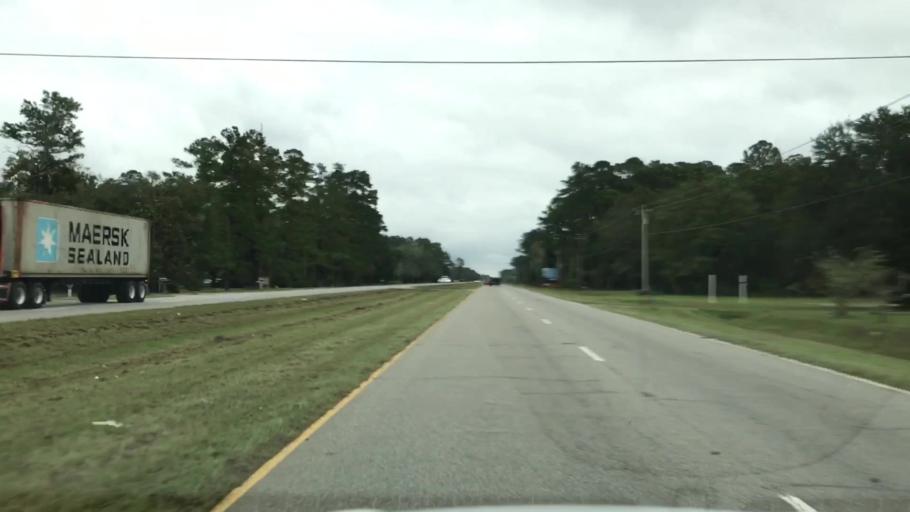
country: US
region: South Carolina
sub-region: Georgetown County
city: Georgetown
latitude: 33.3108
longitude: -79.3313
